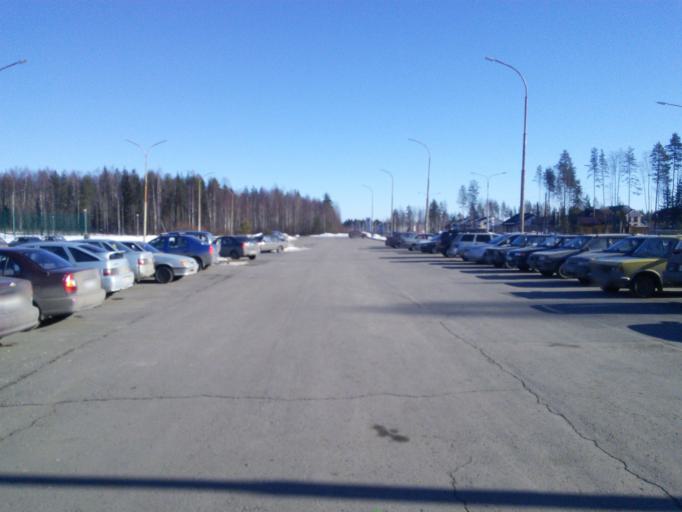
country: RU
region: Republic of Karelia
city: Petrozavodsk
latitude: 61.7717
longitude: 34.2843
